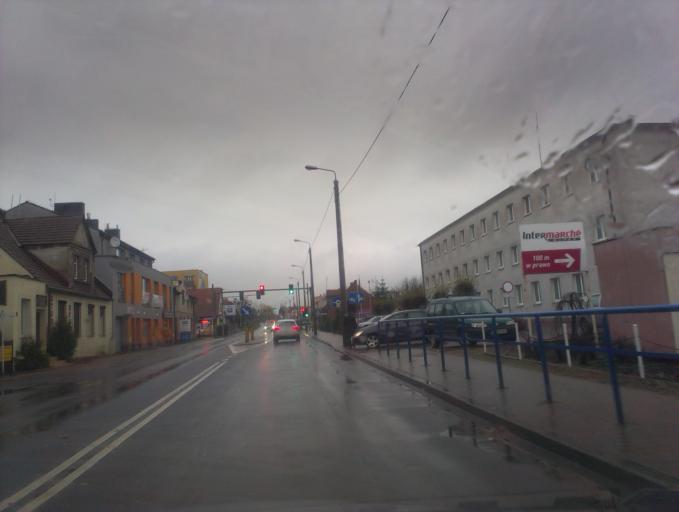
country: PL
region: Greater Poland Voivodeship
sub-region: Powiat obornicki
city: Oborniki
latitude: 52.6473
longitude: 16.8167
